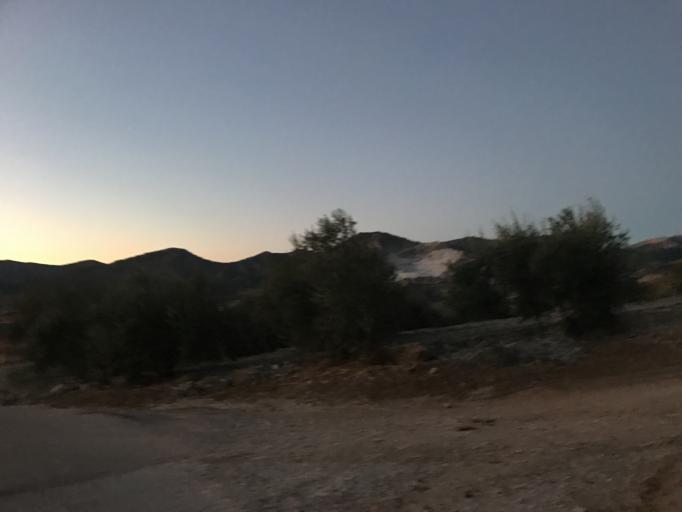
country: ES
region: Andalusia
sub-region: Provincia de Granada
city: Beas de Granada
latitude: 37.2150
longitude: -3.4728
